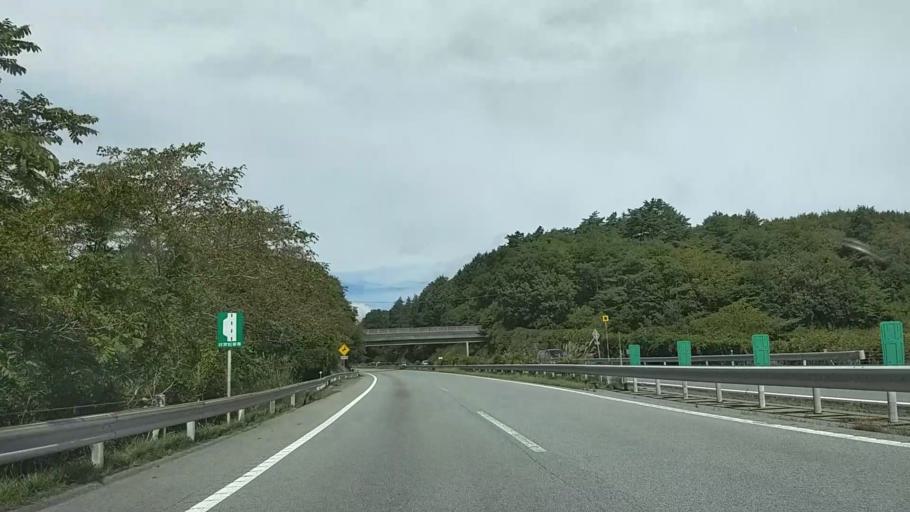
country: JP
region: Yamanashi
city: Nirasaki
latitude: 35.8650
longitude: 138.3250
